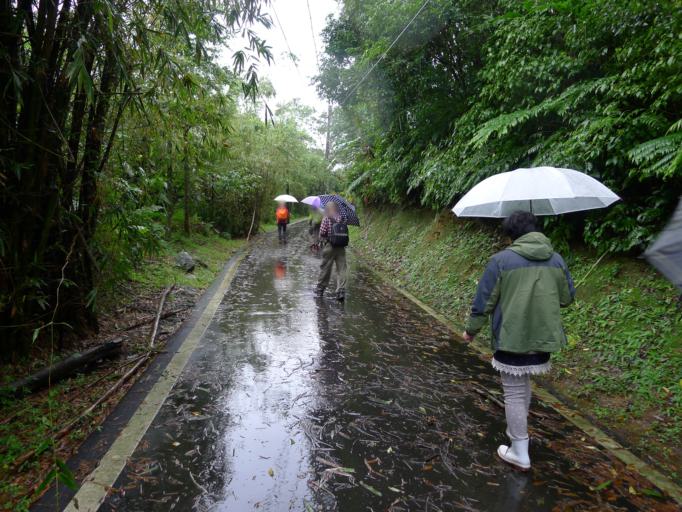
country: TW
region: Taiwan
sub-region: Keelung
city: Keelung
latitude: 25.0210
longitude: 121.9155
